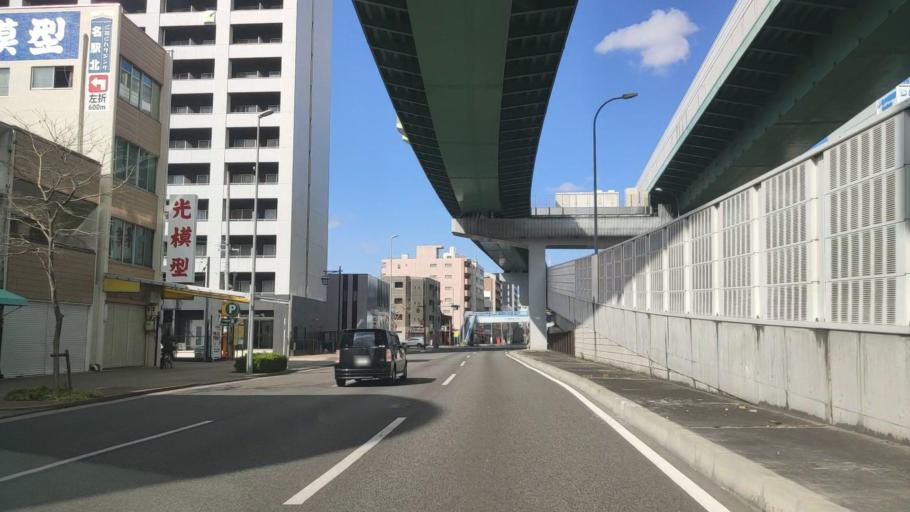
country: JP
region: Aichi
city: Nagoya-shi
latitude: 35.1790
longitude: 136.8898
